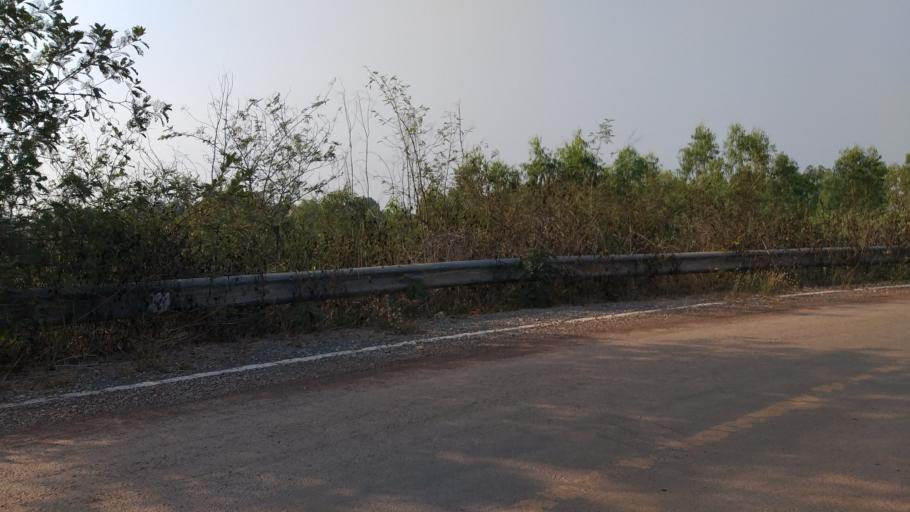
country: TH
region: Changwat Udon Thani
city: Ban Dung
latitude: 17.7438
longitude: 103.3555
